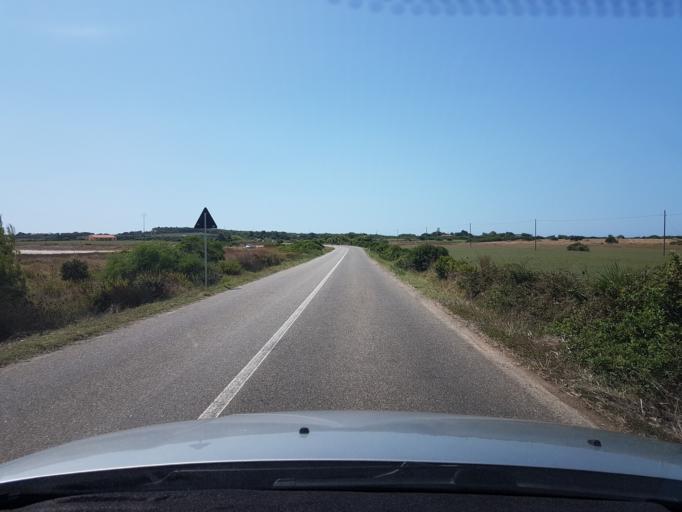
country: IT
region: Sardinia
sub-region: Provincia di Oristano
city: Riola Sardo
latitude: 40.0253
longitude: 8.4386
